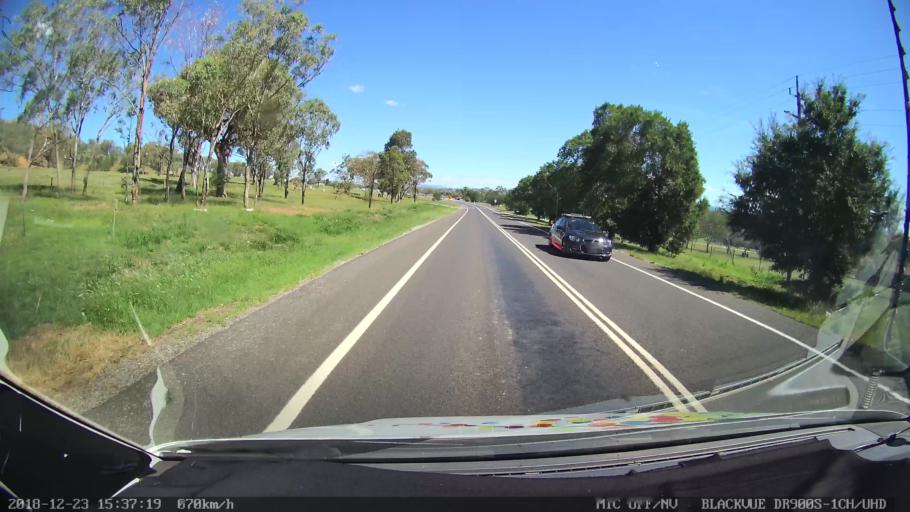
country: AU
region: New South Wales
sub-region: Tamworth Municipality
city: Tamworth
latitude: -31.0508
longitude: 150.8897
